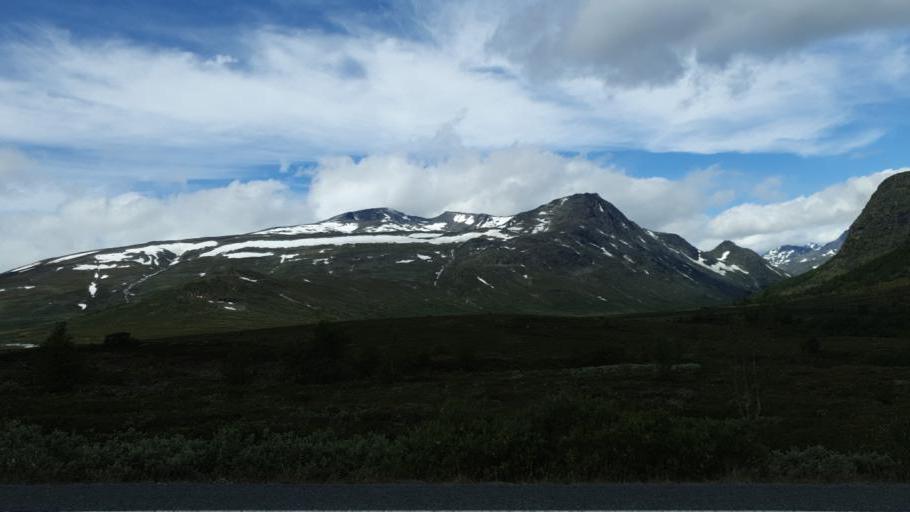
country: NO
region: Oppland
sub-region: Vang
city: Vang
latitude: 61.4618
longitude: 8.8064
